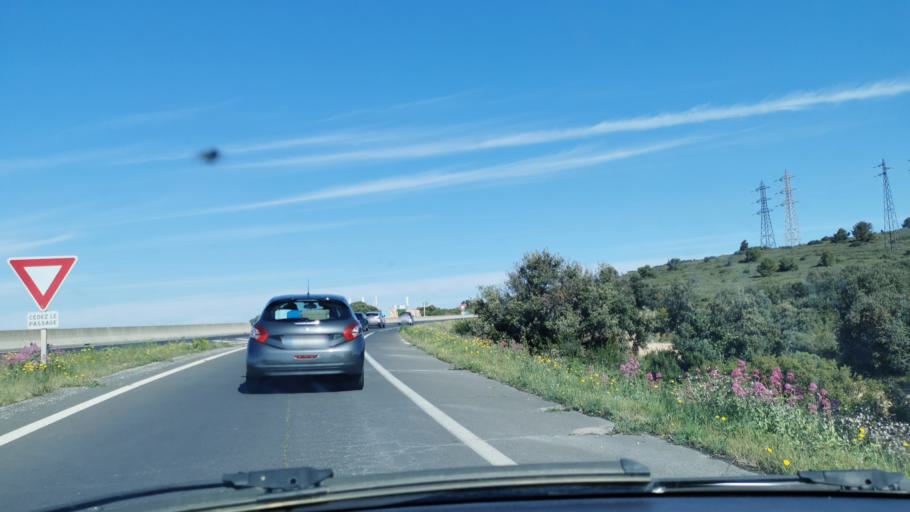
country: FR
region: Languedoc-Roussillon
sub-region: Departement de l'Herault
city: Balaruc-le-Vieux
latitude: 43.4470
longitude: 3.7096
